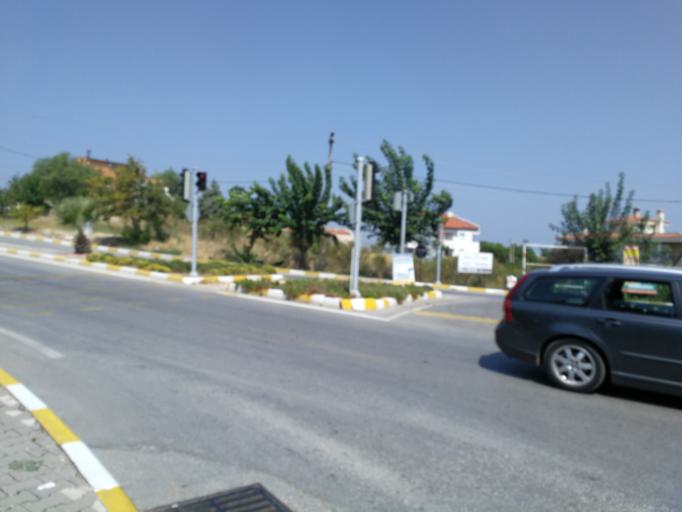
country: TR
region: Izmir
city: Urla
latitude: 38.3266
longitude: 26.7723
